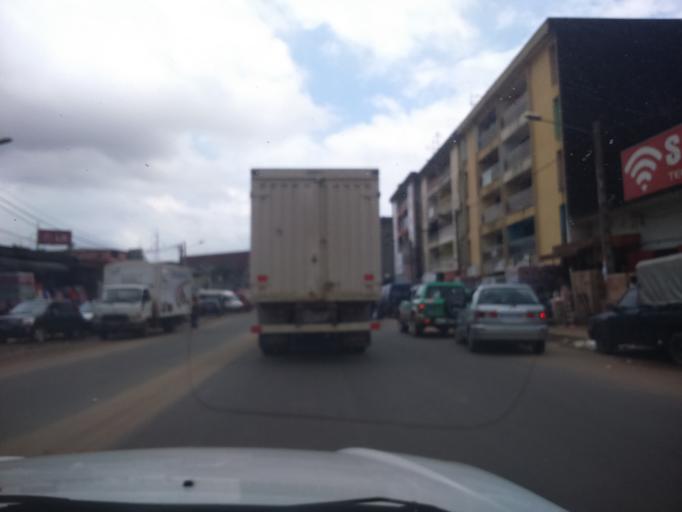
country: CI
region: Lagunes
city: Abidjan
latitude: 5.3549
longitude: -4.0652
